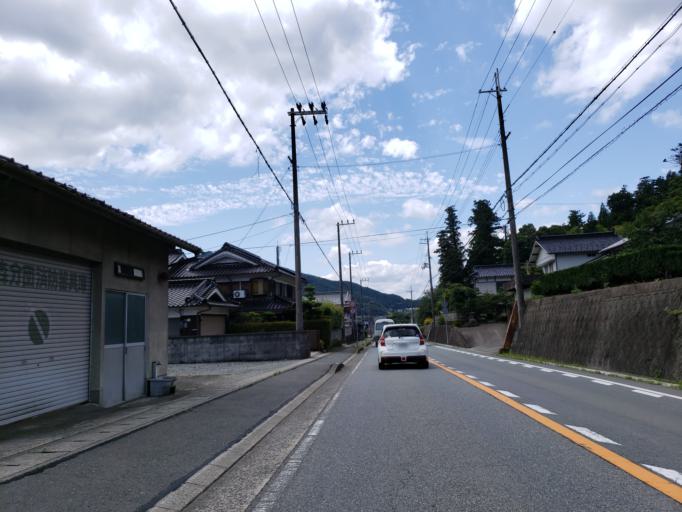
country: JP
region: Hyogo
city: Yamazakicho-nakabirose
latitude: 34.9859
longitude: 134.6022
